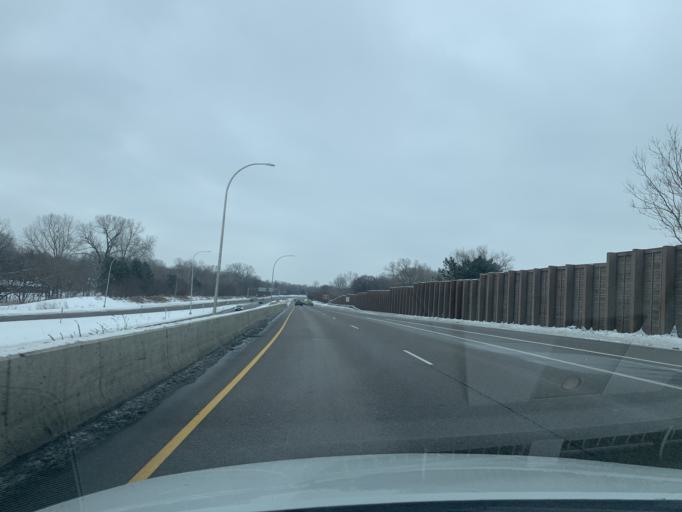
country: US
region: Minnesota
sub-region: Anoka County
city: Coon Rapids
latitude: 45.1173
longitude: -93.3071
